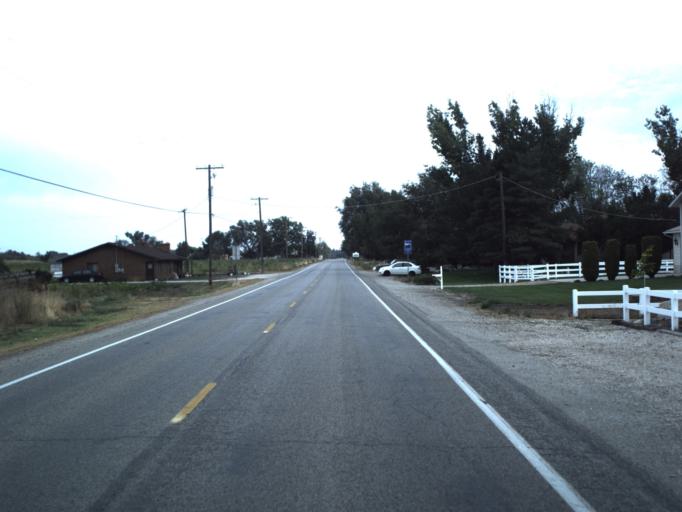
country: US
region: Utah
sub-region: Weber County
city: Plain City
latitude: 41.2624
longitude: -112.0924
